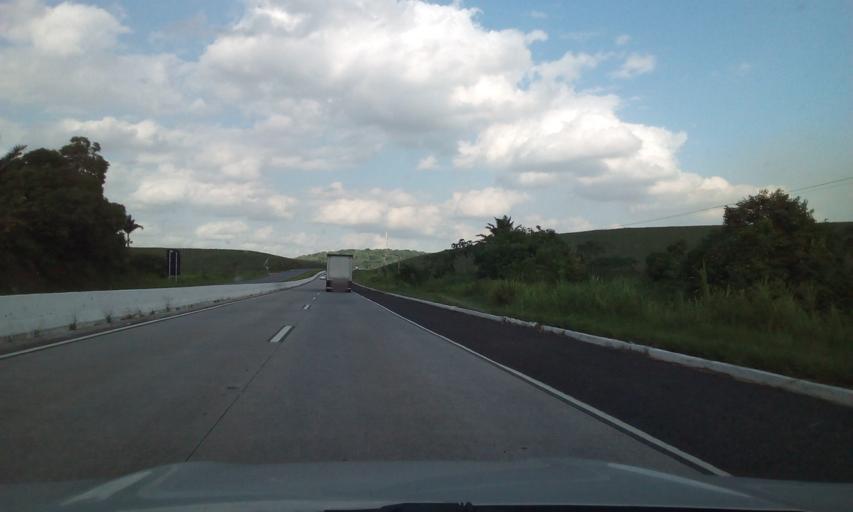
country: BR
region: Pernambuco
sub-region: Joaquim Nabuco
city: Joaquim Nabuco
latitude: -8.5905
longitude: -35.5143
